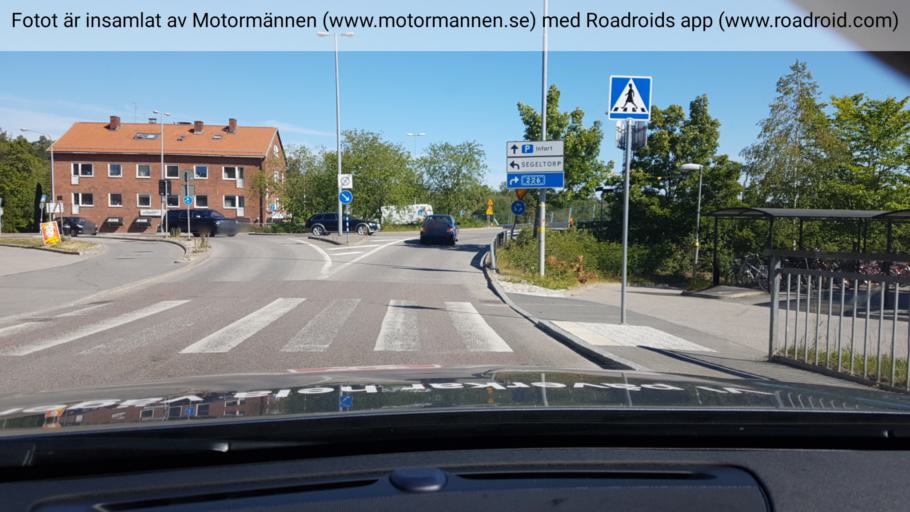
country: SE
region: Stockholm
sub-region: Huddinge Kommun
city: Huddinge
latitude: 59.2530
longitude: 17.9951
